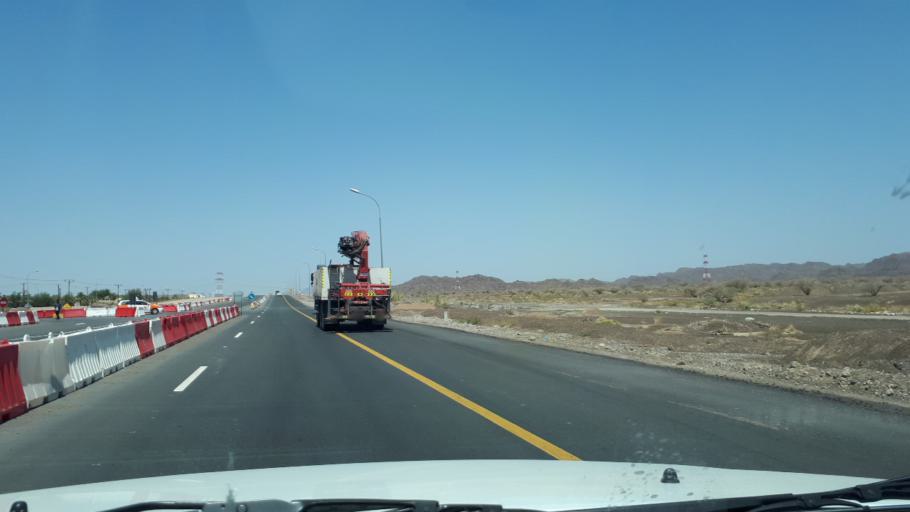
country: OM
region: Ash Sharqiyah
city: Al Qabil
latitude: 22.6448
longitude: 58.6300
